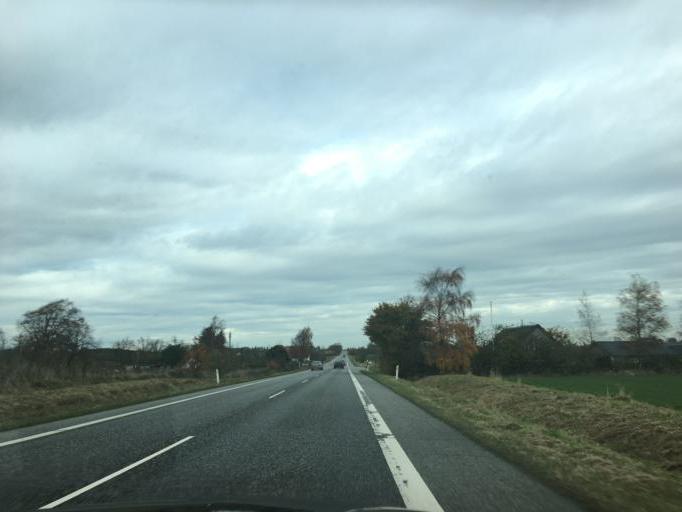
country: DK
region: South Denmark
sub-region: Vejle Kommune
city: Vejle
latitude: 55.6394
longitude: 9.4971
